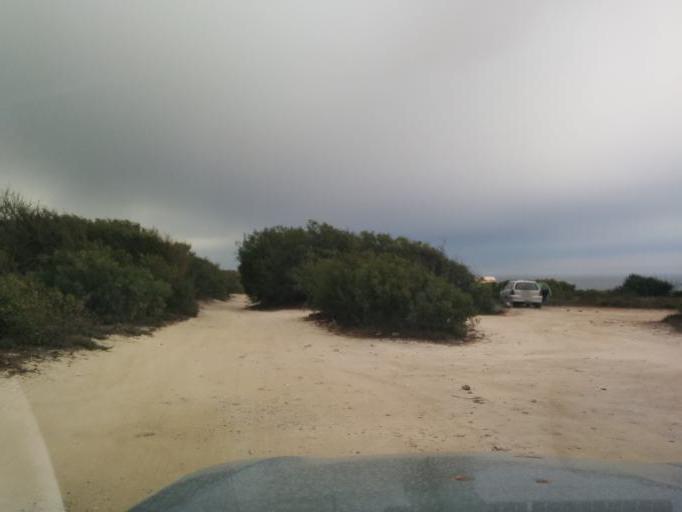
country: PT
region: Beja
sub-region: Odemira
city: Sao Teotonio
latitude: 37.5192
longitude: -8.7854
